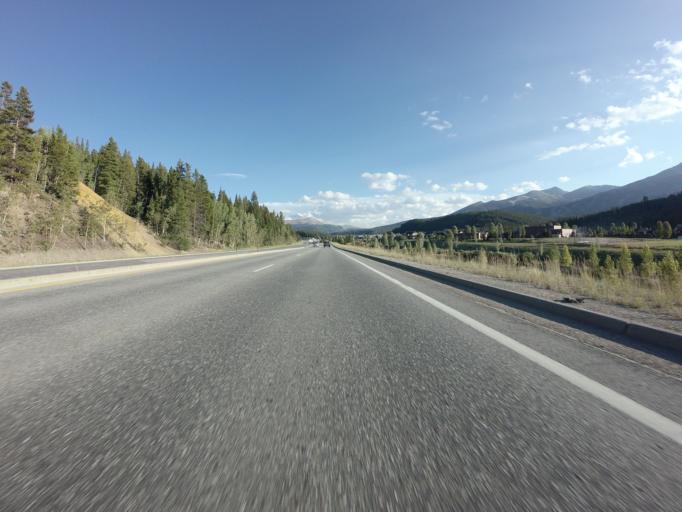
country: US
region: Colorado
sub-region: Summit County
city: Breckenridge
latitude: 39.5026
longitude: -106.0474
